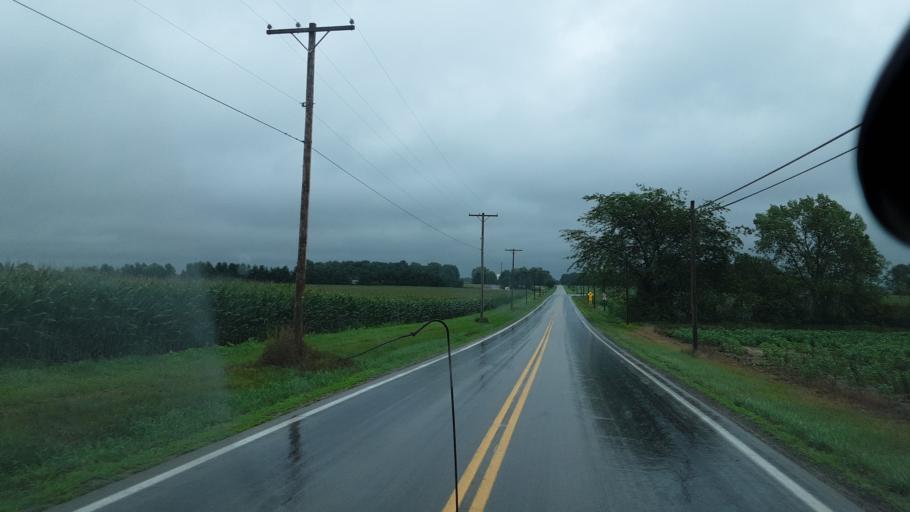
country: US
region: Ohio
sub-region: Mercer County
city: Rockford
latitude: 40.7498
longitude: -84.7811
